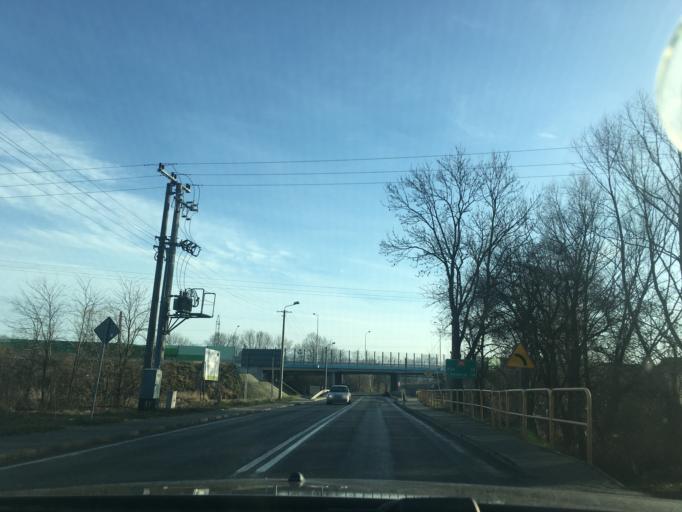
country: PL
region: Swietokrzyskie
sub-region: Powiat jedrzejowski
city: Jedrzejow
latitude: 50.6347
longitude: 20.3154
